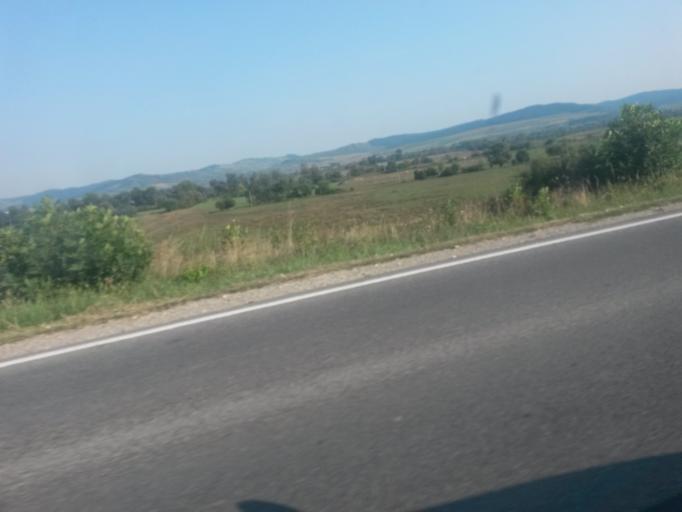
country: RO
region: Alba
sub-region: Comuna Unirea
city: Unirea
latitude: 46.3910
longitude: 23.7896
